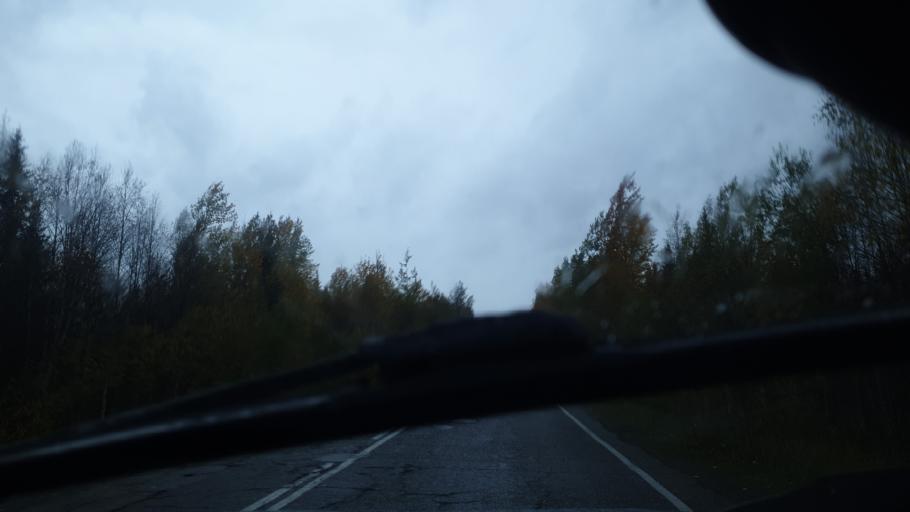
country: RU
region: Komi Republic
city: Nizhniy Odes
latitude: 63.6243
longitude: 55.1960
